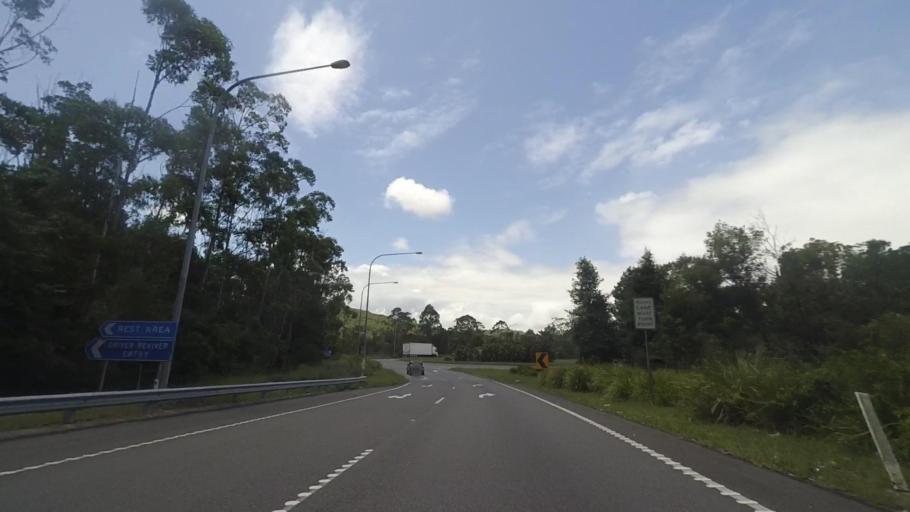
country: AU
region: New South Wales
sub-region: Gosford Shire
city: Lisarow
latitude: -33.3450
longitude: 151.3680
